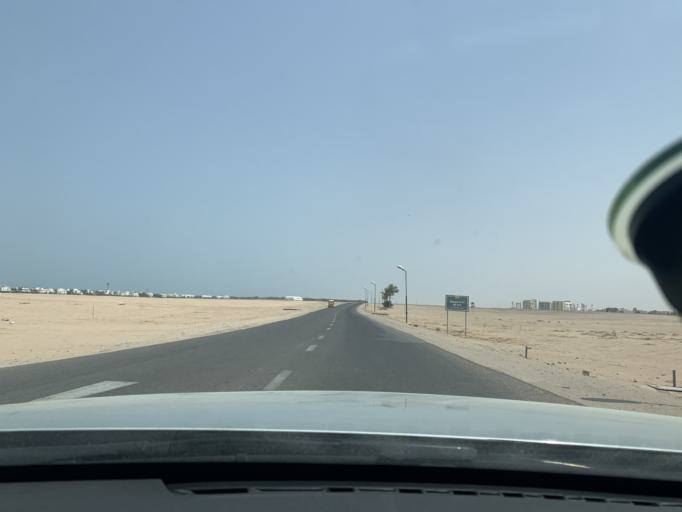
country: EG
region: Red Sea
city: El Gouna
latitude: 27.3754
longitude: 33.6601
